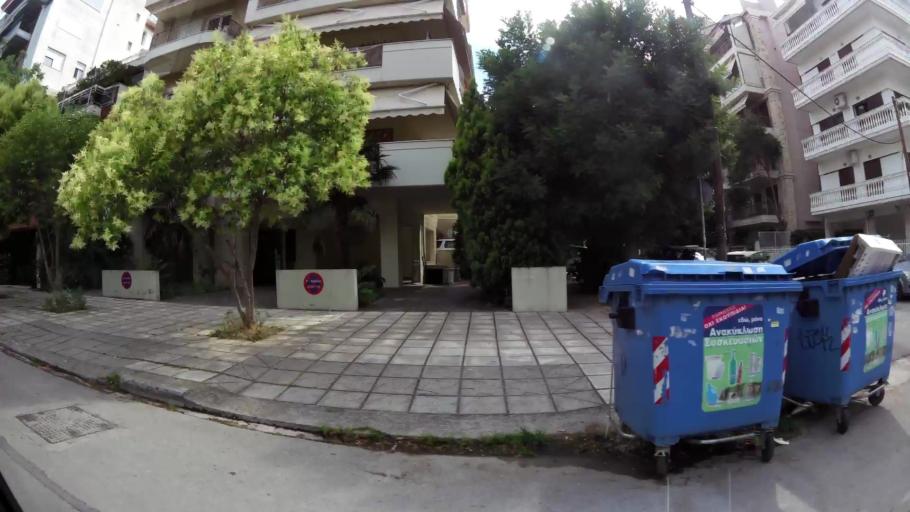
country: GR
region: Central Macedonia
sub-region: Nomos Thessalonikis
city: Kalamaria
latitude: 40.5886
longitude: 22.9504
